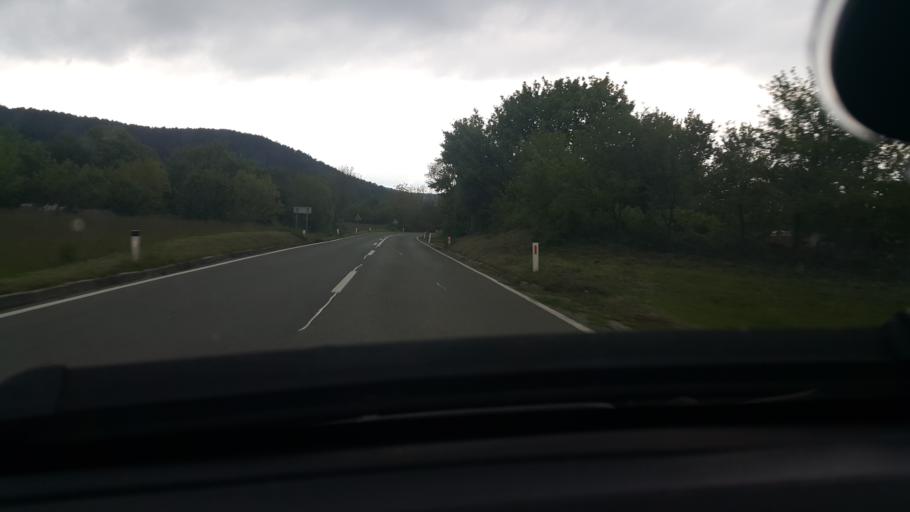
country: SI
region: Divaca
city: Divaca
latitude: 45.7023
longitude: 13.9307
